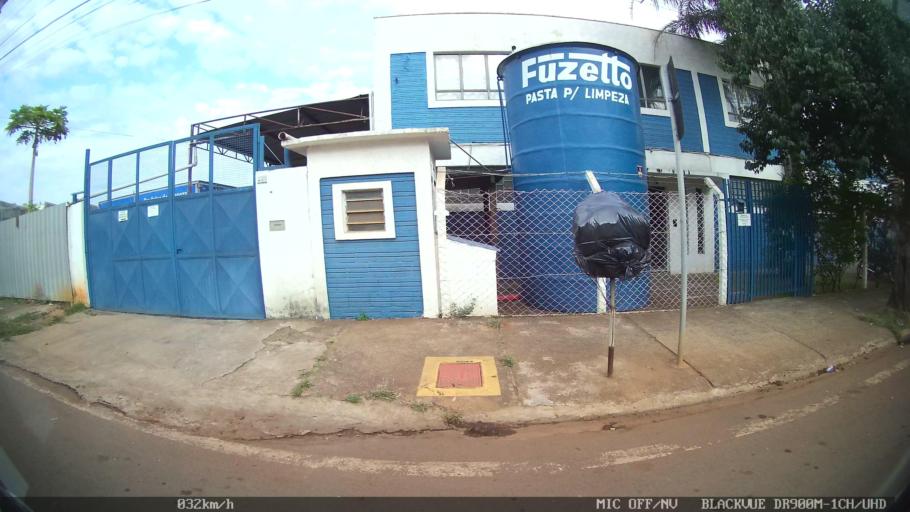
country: BR
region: Sao Paulo
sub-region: Santa Barbara D'Oeste
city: Santa Barbara d'Oeste
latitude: -22.7617
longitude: -47.3896
